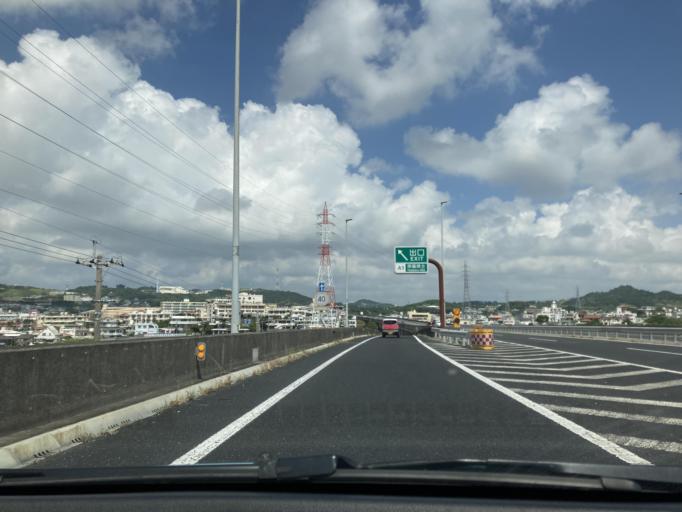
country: JP
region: Okinawa
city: Tomigusuku
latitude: 26.1945
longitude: 127.7394
